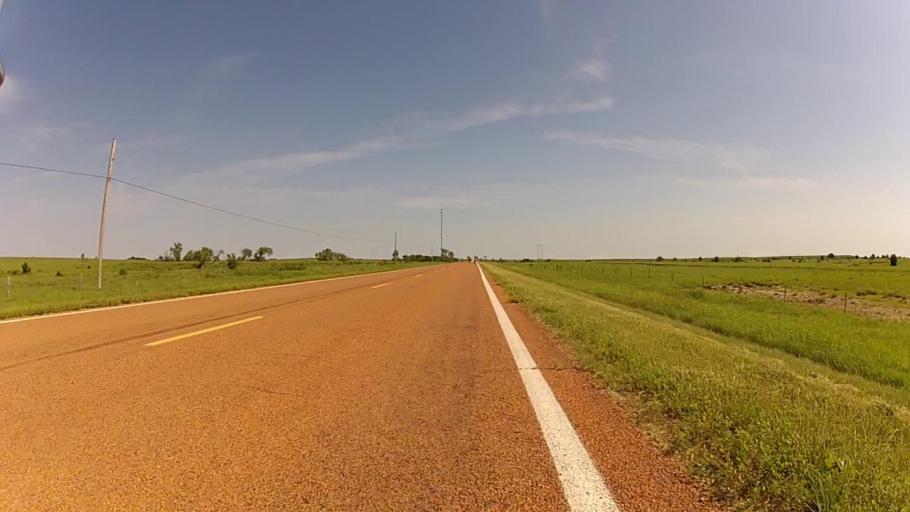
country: US
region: Kansas
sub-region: Cowley County
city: Winfield
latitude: 37.1050
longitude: -96.6436
